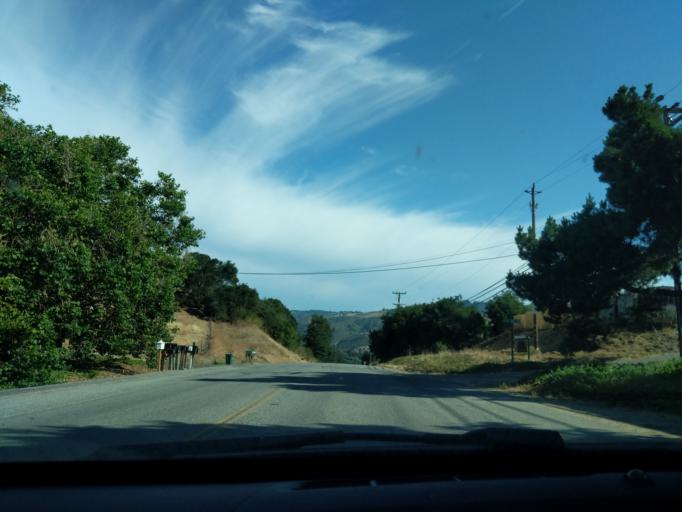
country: US
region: California
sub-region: San Benito County
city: Aromas
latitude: 36.8816
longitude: -121.6416
